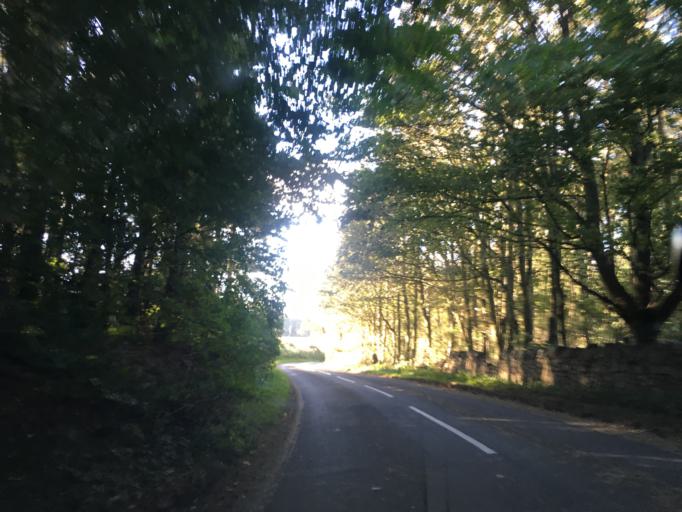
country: GB
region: Scotland
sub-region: East Lothian
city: Pencaitland
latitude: 55.8672
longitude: -2.8877
